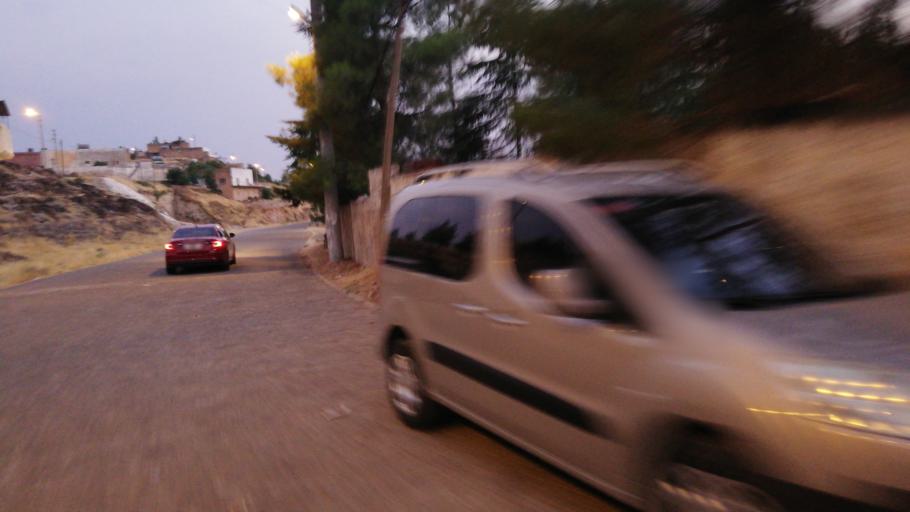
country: TR
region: Mardin
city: Kindirip
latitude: 37.4507
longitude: 41.2221
